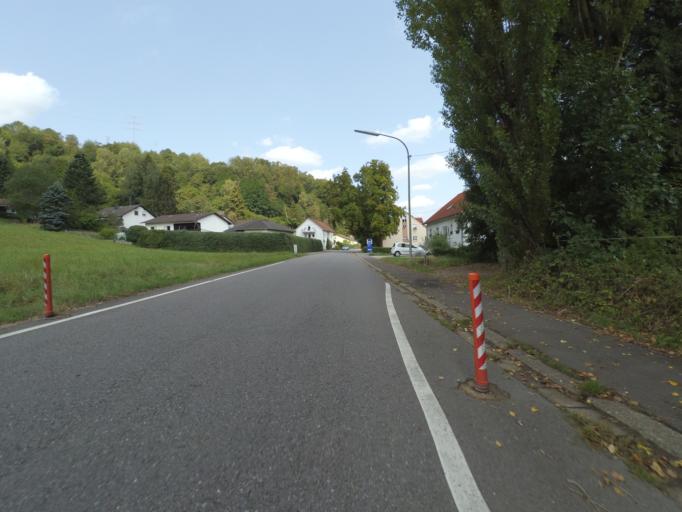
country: DE
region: Saarland
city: Merzig
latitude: 49.4594
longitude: 6.6721
